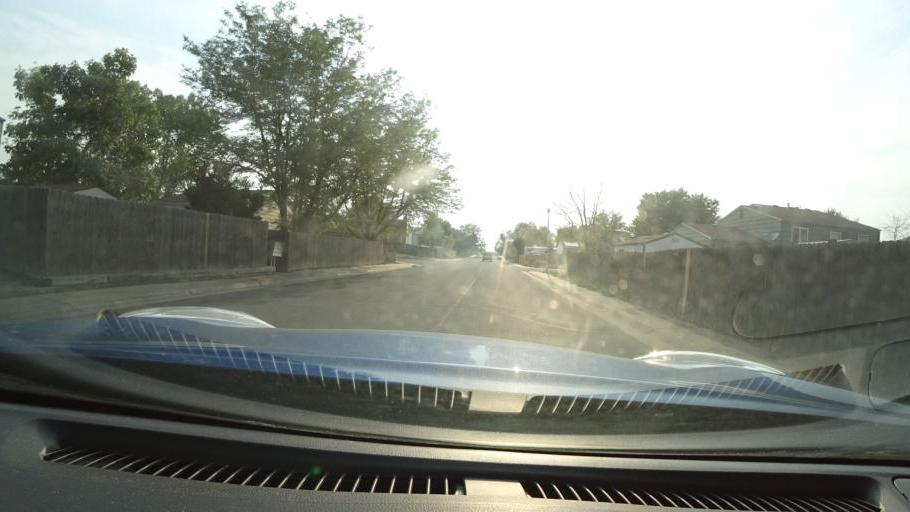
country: US
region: Colorado
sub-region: Adams County
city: Aurora
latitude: 39.7456
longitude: -104.7654
